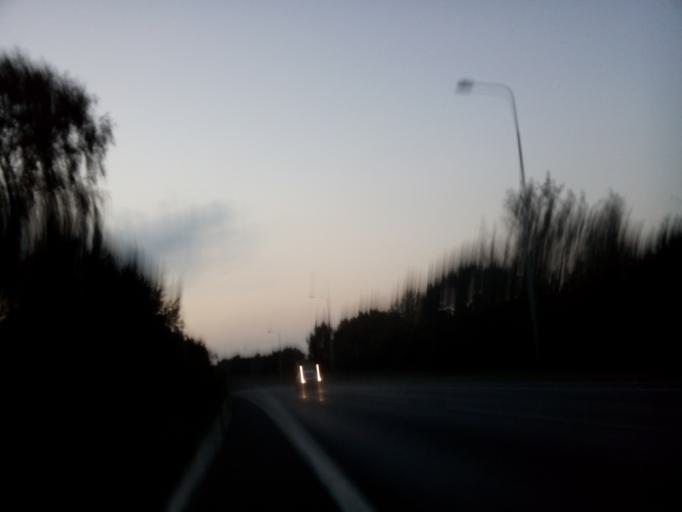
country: GB
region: England
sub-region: Suffolk
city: Kesgrave
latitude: 52.0342
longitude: 1.2131
